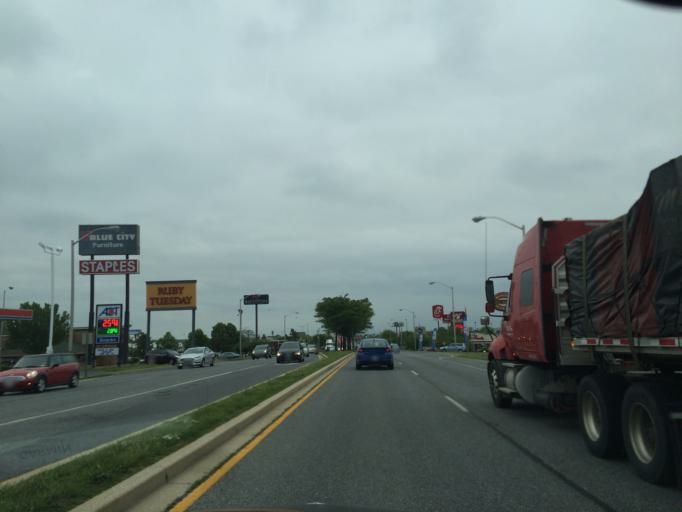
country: US
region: Maryland
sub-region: Washington County
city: Halfway
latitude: 39.6318
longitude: -77.7606
